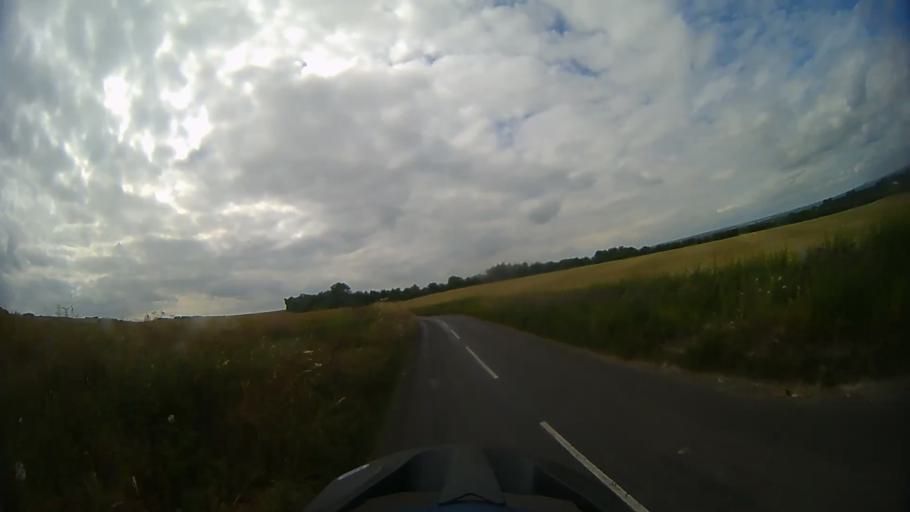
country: GB
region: England
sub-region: Oxfordshire
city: Stanford in the Vale
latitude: 51.5808
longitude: -1.4898
